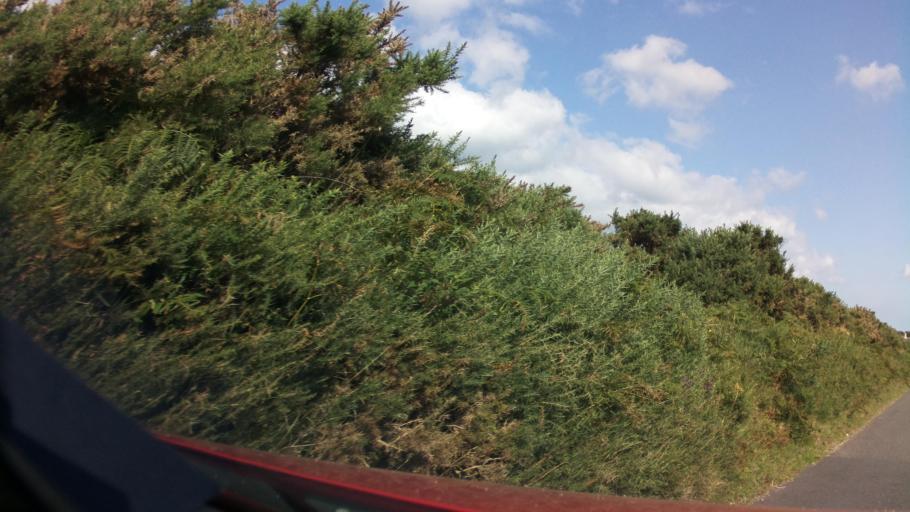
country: GB
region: England
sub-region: Devon
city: Buckfastleigh
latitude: 50.5464
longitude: -3.8571
